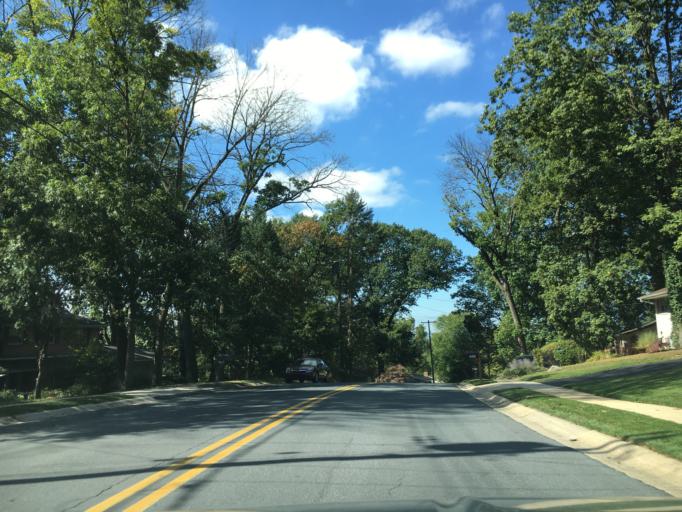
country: US
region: Pennsylvania
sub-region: York County
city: East York
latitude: 39.9624
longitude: -76.6706
